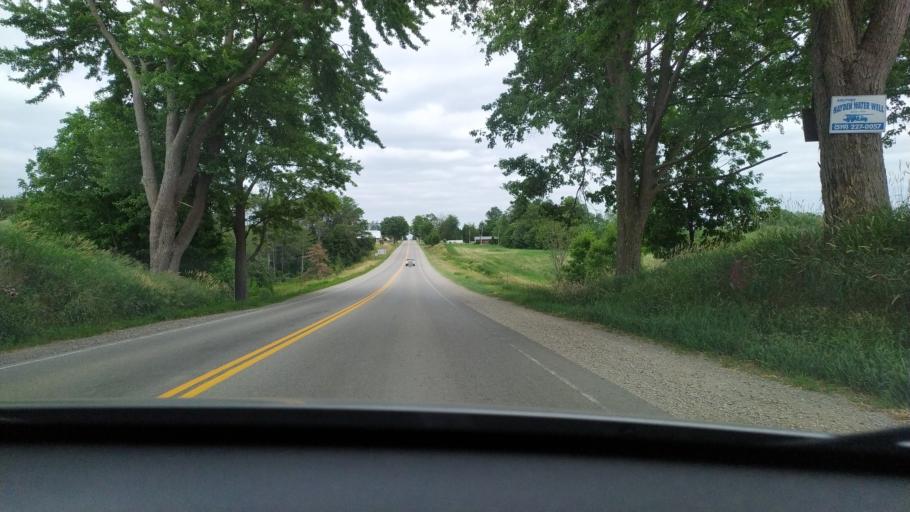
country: CA
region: Ontario
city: Stratford
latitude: 43.3158
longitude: -80.9620
